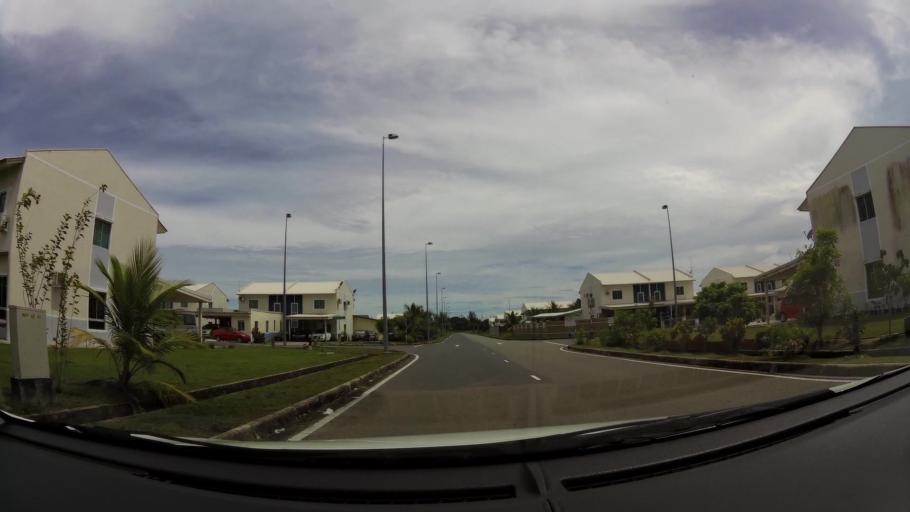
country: BN
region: Belait
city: Kuala Belait
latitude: 4.5867
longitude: 114.2664
